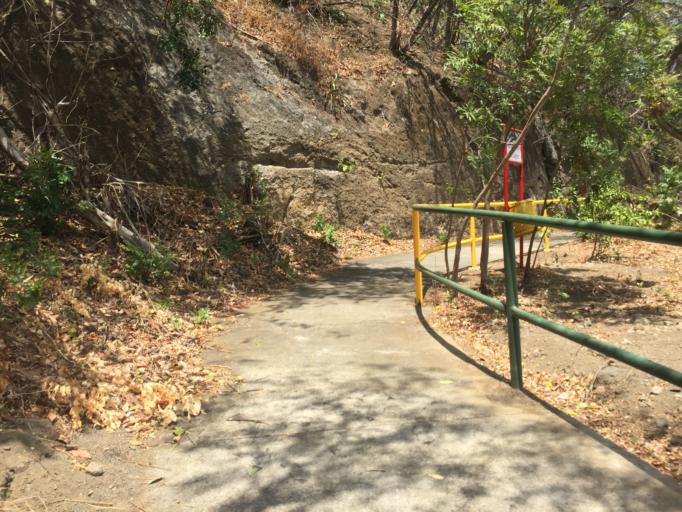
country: NI
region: Managua
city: Managua
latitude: 12.1382
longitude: -86.2725
